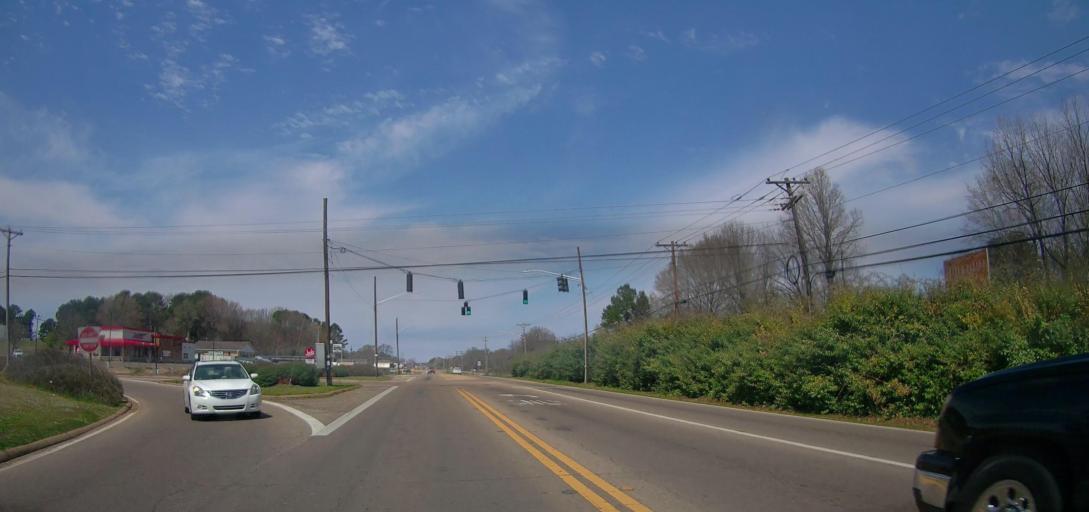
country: US
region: Mississippi
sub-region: Union County
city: New Albany
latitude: 34.4997
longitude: -89.0244
